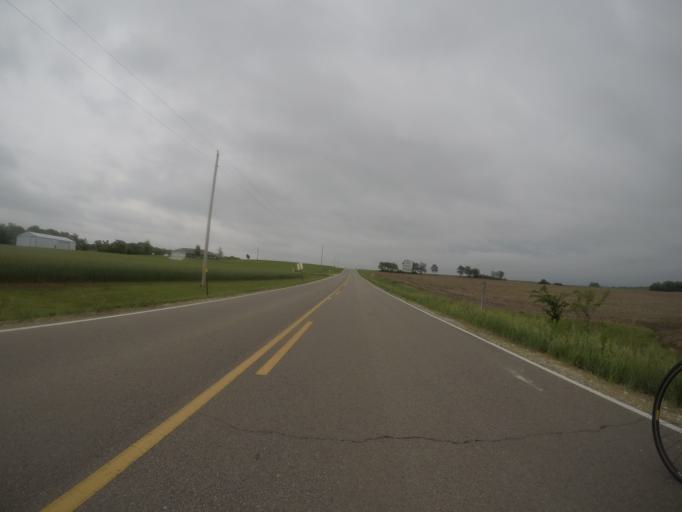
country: US
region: Kansas
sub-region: Pottawatomie County
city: Westmoreland
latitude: 39.5115
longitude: -96.2090
